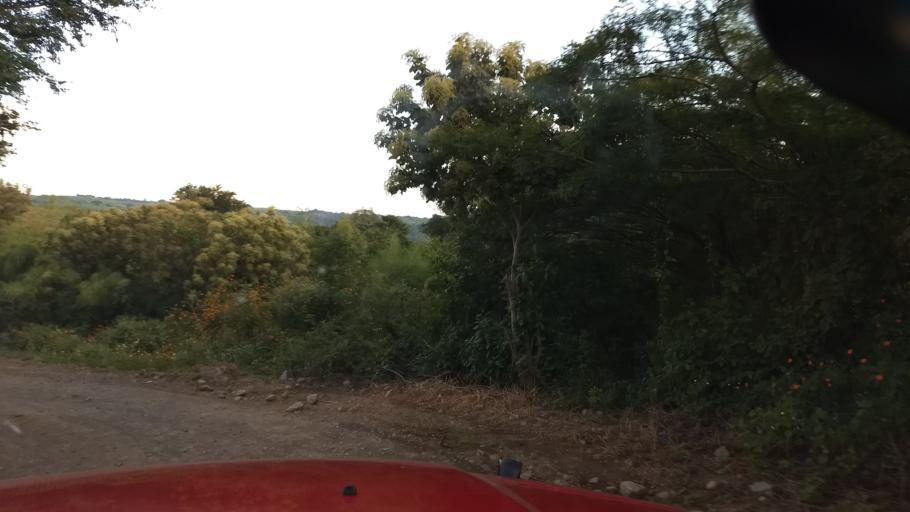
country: MX
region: Colima
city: Suchitlan
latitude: 19.4890
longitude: -103.7902
